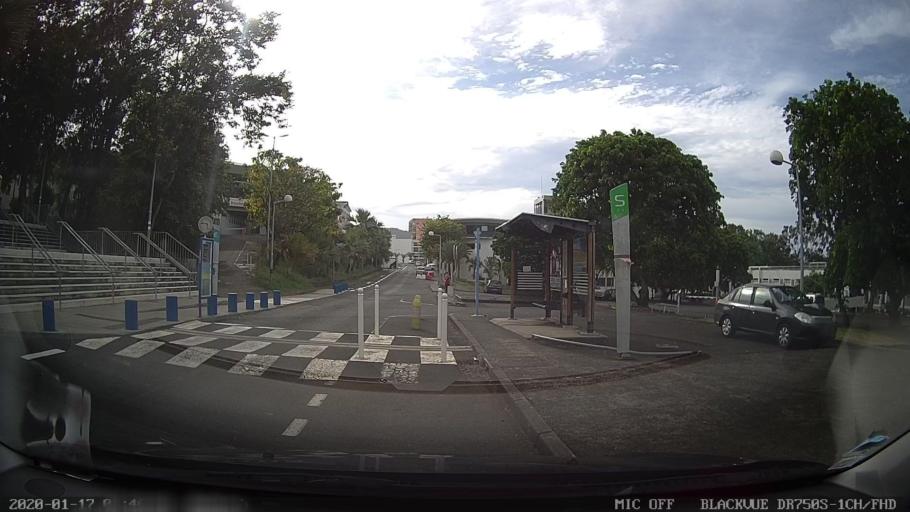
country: RE
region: Reunion
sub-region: Reunion
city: Saint-Denis
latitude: -20.9019
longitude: 55.4849
